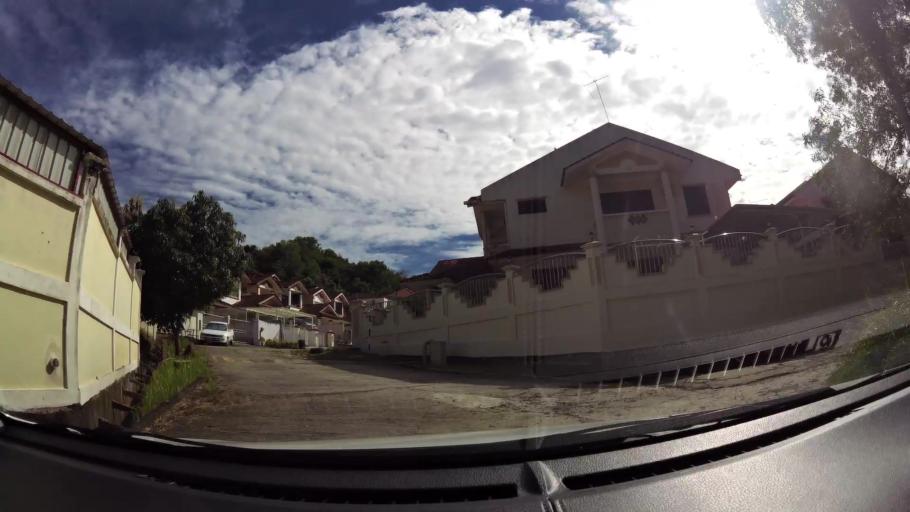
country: BN
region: Brunei and Muara
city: Bandar Seri Begawan
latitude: 4.9033
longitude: 114.9734
